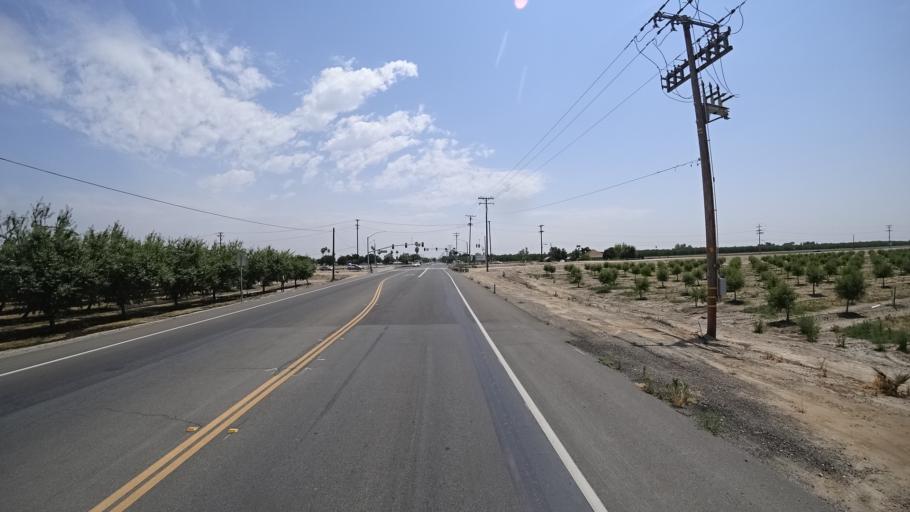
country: US
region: California
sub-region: Kings County
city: Armona
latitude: 36.3281
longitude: -119.6926
